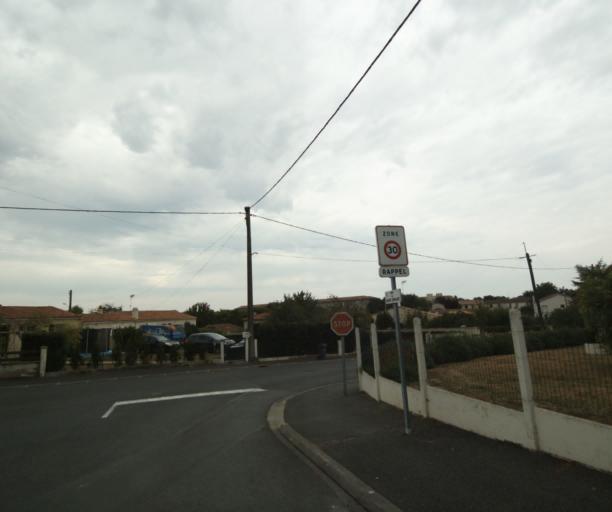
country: FR
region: Poitou-Charentes
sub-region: Departement de la Charente-Maritime
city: Tonnay-Charente
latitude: 45.9472
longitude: -0.8866
